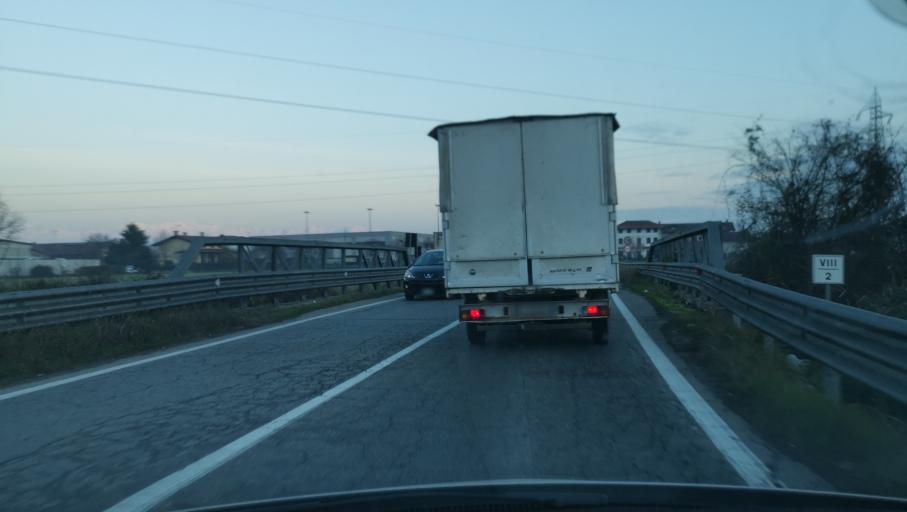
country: IT
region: Piedmont
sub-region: Provincia di Torino
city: Chivasso
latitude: 45.2132
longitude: 7.8903
